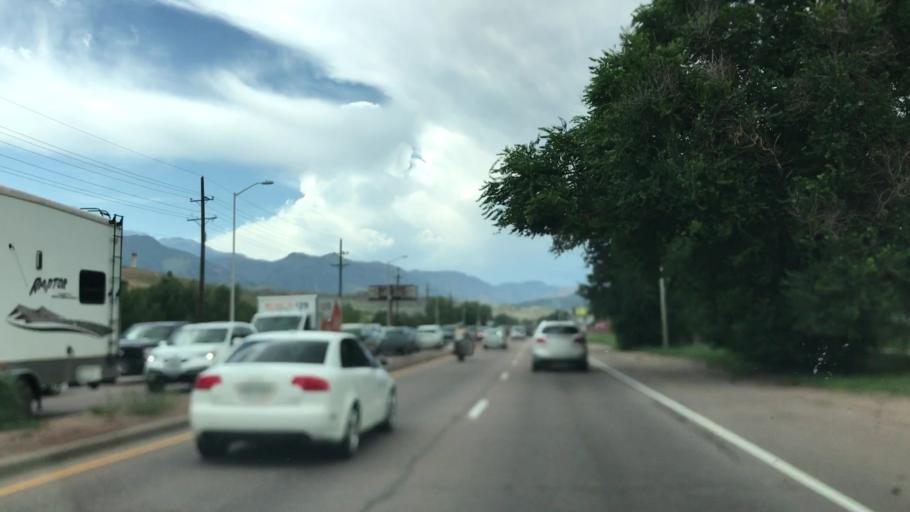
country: US
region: Colorado
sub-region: El Paso County
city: Colorado Springs
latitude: 38.8329
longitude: -104.8438
